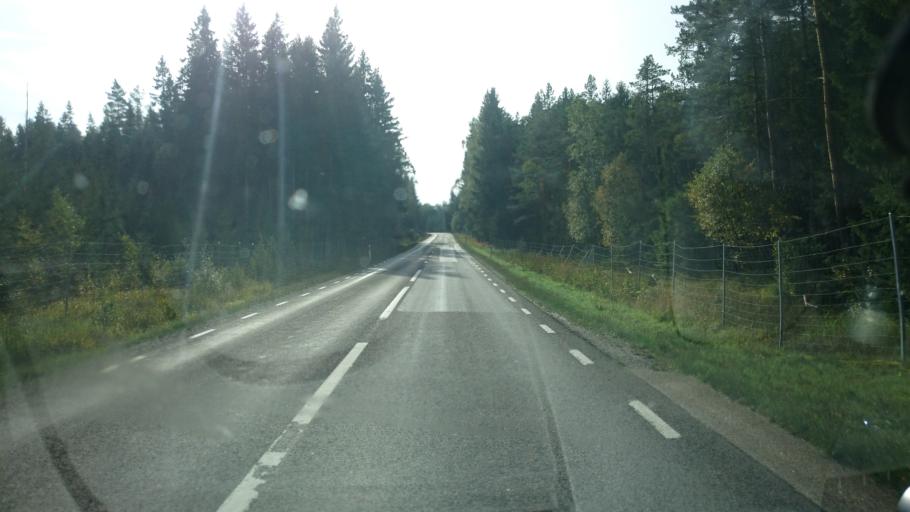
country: SE
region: Vaestra Goetaland
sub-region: Alingsas Kommun
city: Sollebrunn
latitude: 58.1443
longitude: 12.4194
